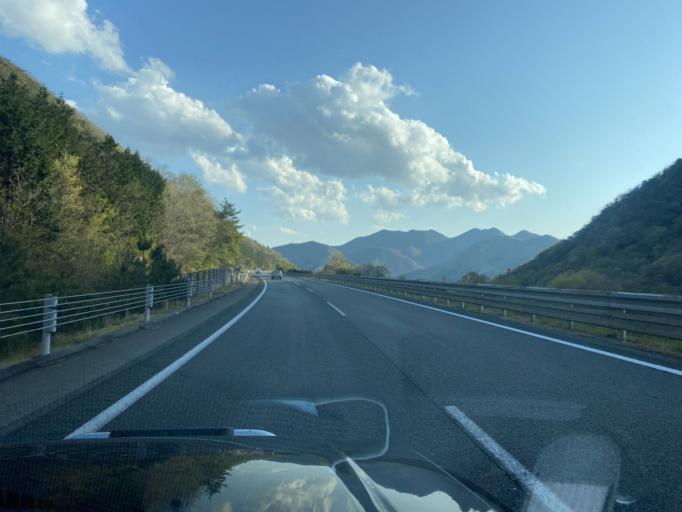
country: JP
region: Hyogo
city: Sasayama
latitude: 35.0129
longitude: 135.1627
